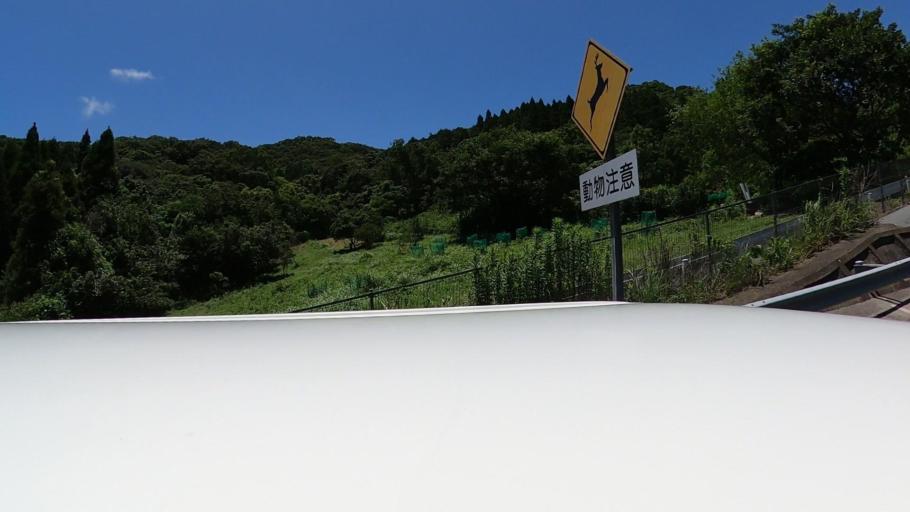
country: JP
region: Miyazaki
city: Nobeoka
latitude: 32.4043
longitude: 131.6145
